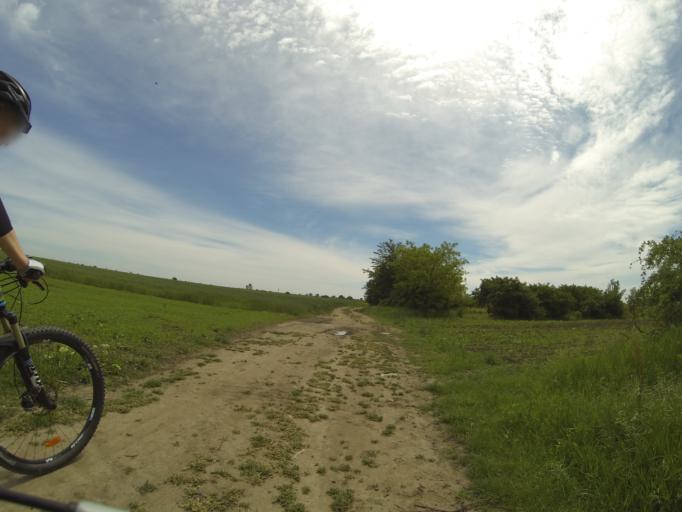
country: RO
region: Dolj
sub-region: Comuna Leu
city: Leu
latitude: 44.2017
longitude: 23.9974
